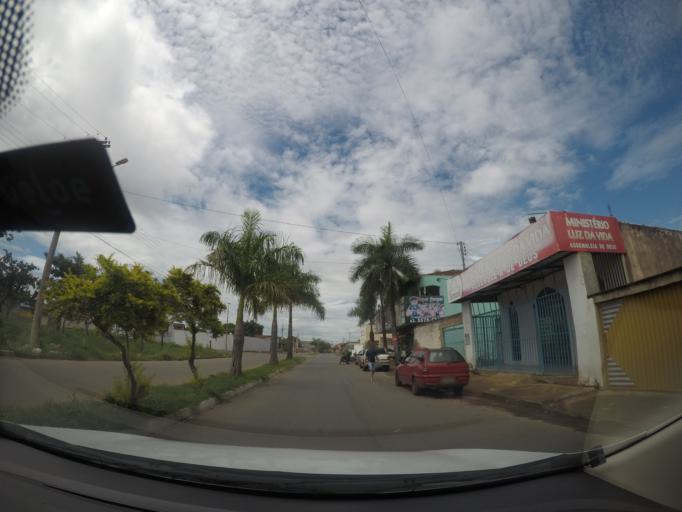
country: BR
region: Goias
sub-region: Aparecida De Goiania
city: Aparecida de Goiania
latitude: -16.7599
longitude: -49.3522
